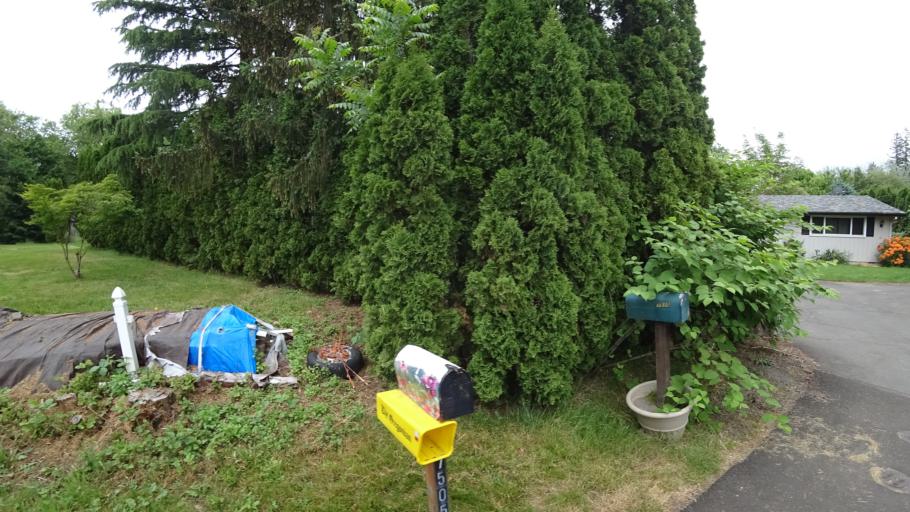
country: US
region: Oregon
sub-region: Washington County
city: Garden Home-Whitford
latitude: 45.4637
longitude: -122.7541
